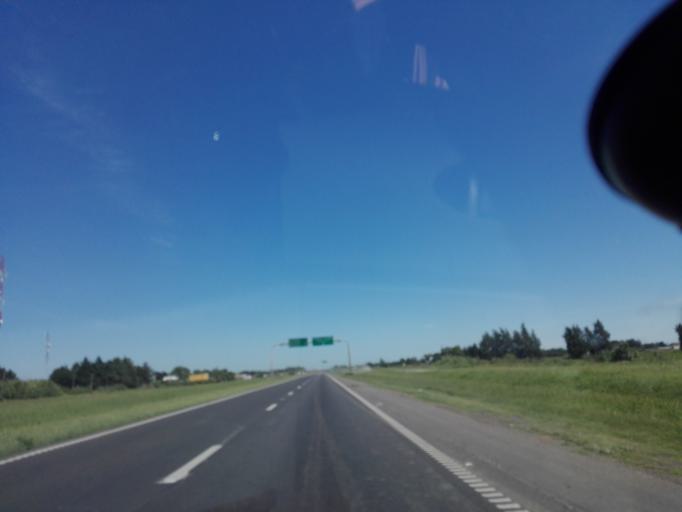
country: AR
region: Buenos Aires
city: San Nicolas de los Arroyos
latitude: -33.3698
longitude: -60.2473
